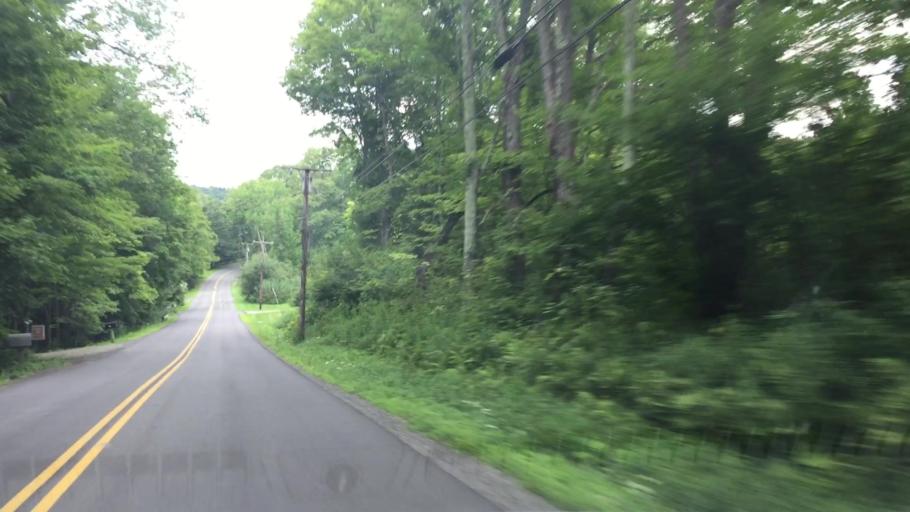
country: US
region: Massachusetts
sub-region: Berkshire County
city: Housatonic
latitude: 42.2735
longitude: -73.4091
